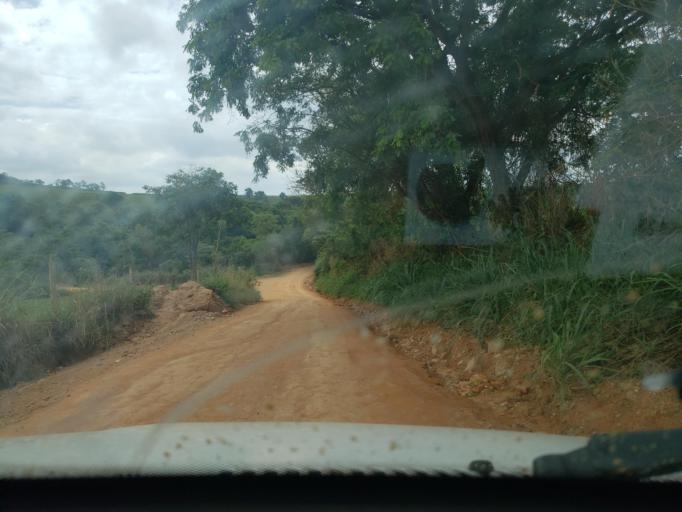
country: BR
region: Minas Gerais
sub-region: Boa Esperanca
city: Boa Esperanca
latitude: -20.9775
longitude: -45.6002
